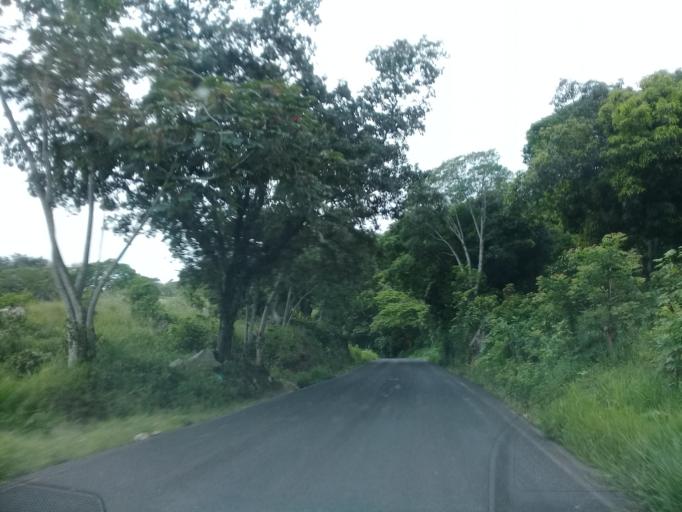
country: MX
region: Veracruz
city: El Castillo
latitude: 19.5617
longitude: -96.8427
